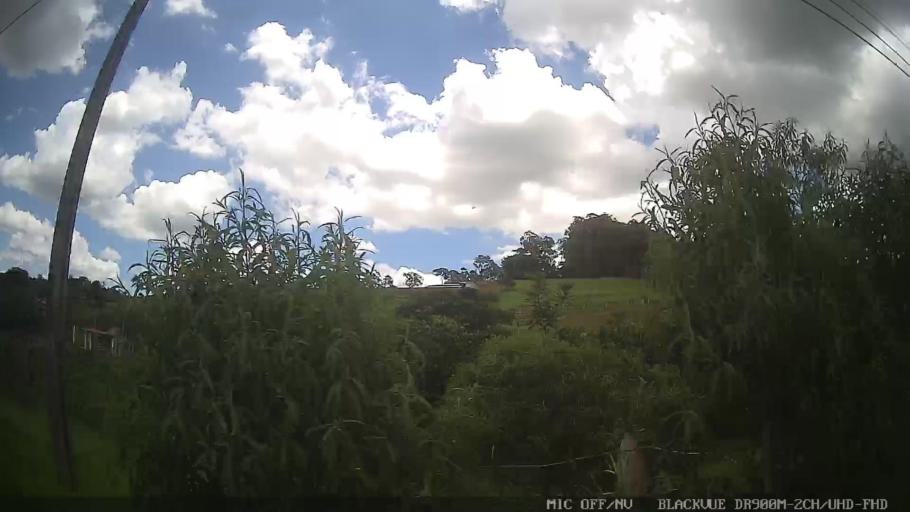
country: BR
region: Sao Paulo
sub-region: Braganca Paulista
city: Braganca Paulista
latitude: -23.0079
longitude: -46.4895
